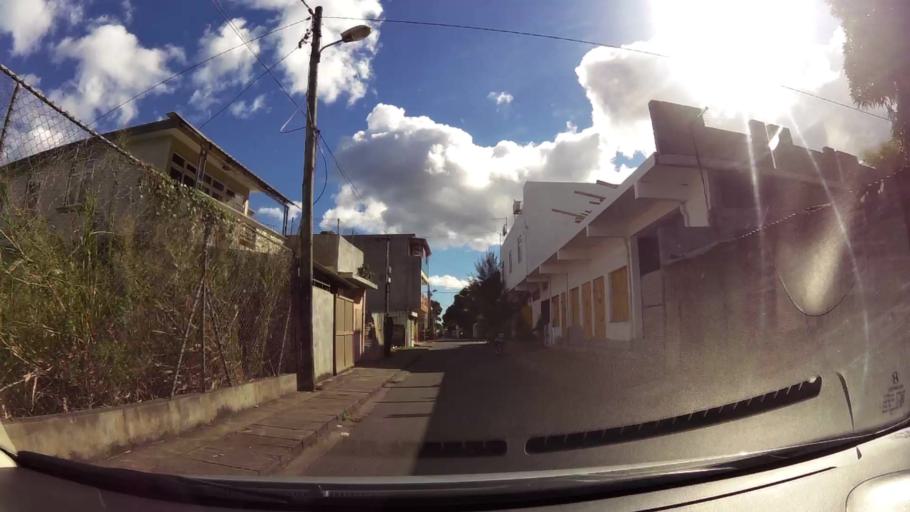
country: MU
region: Pamplemousses
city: Le Hochet
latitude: -20.1457
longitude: 57.5195
